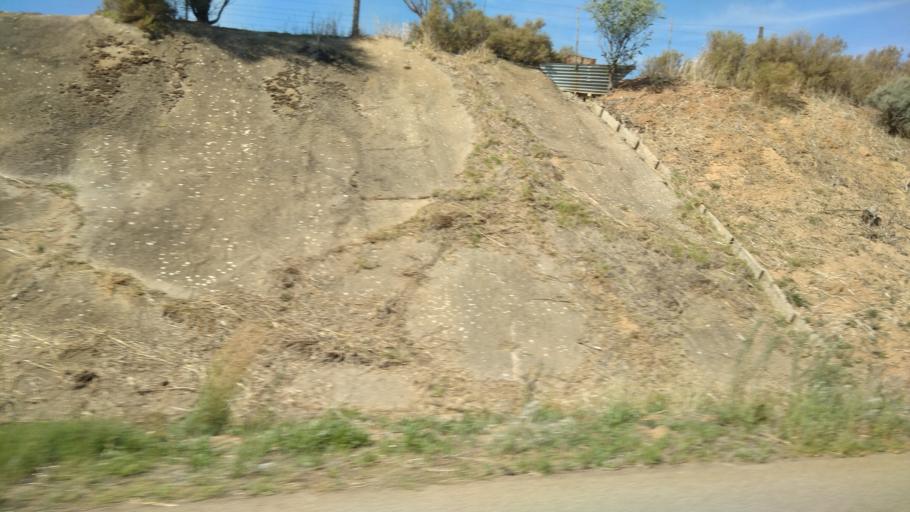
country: ZA
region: Western Cape
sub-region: West Coast District Municipality
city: Malmesbury
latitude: -33.3872
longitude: 18.6710
